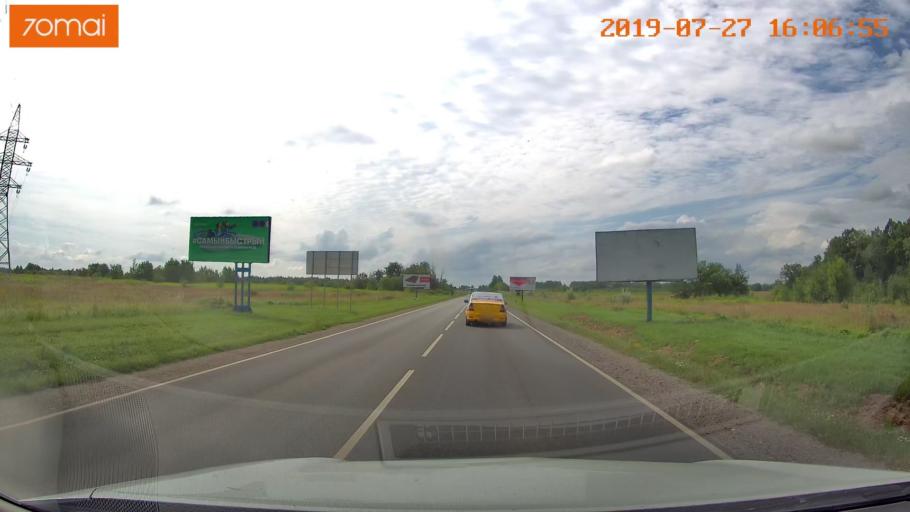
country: RU
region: Kaliningrad
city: Chernyakhovsk
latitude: 54.6345
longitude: 21.7687
